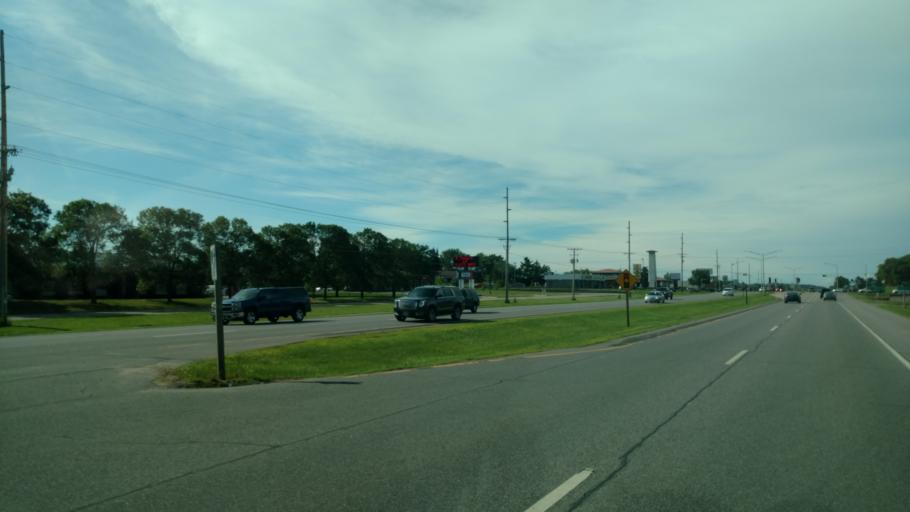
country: US
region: Wisconsin
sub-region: Monroe County
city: Tomah
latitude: 43.9986
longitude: -90.5047
